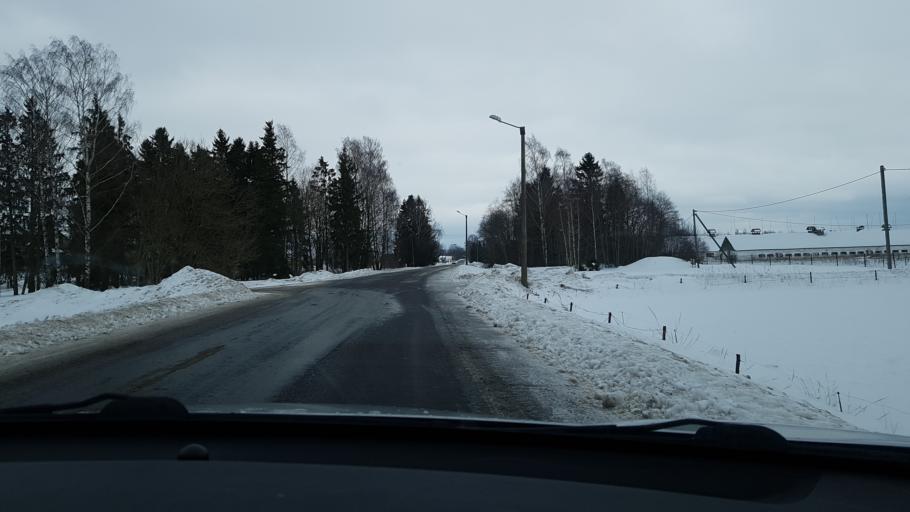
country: EE
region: Jaervamaa
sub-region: Koeru vald
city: Koeru
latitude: 58.9715
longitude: 26.0114
